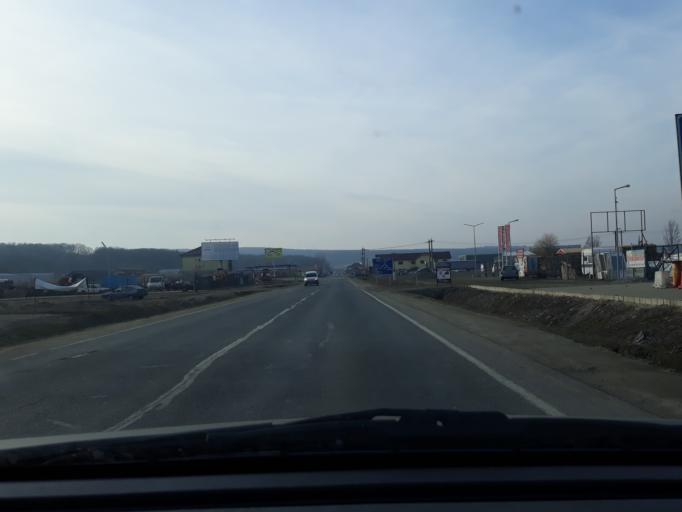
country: RO
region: Salaj
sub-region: Comuna Hereclean
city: Hereclean
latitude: 47.2243
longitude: 23.0243
